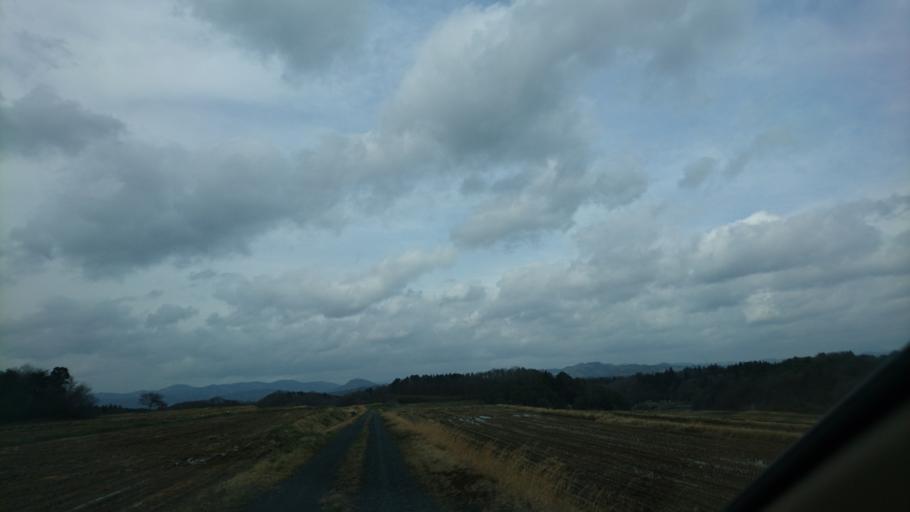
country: JP
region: Iwate
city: Ichinoseki
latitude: 38.8887
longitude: 141.1616
